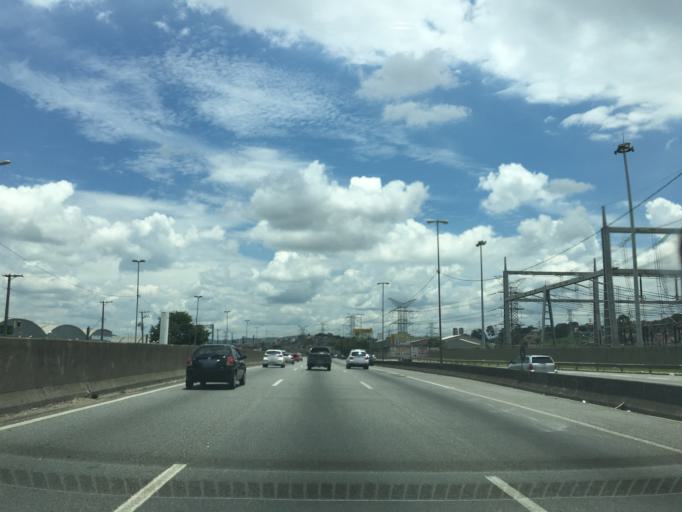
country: BR
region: Sao Paulo
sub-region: Guarulhos
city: Guarulhos
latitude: -23.4830
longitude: -46.5598
